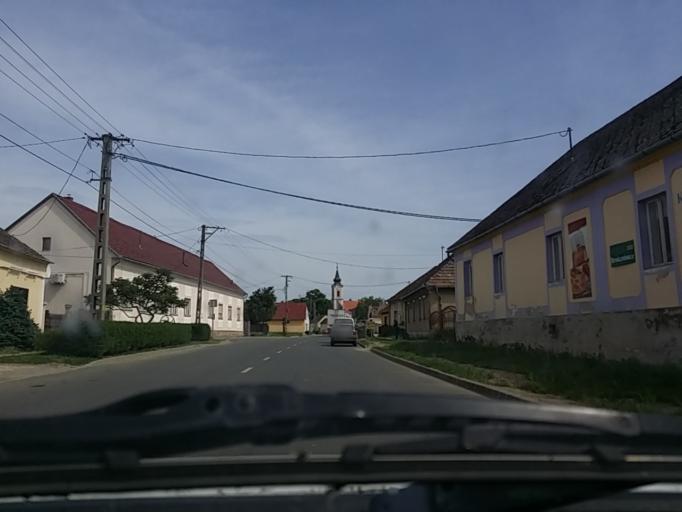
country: HU
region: Baranya
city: Vajszlo
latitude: 45.8609
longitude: 17.9796
